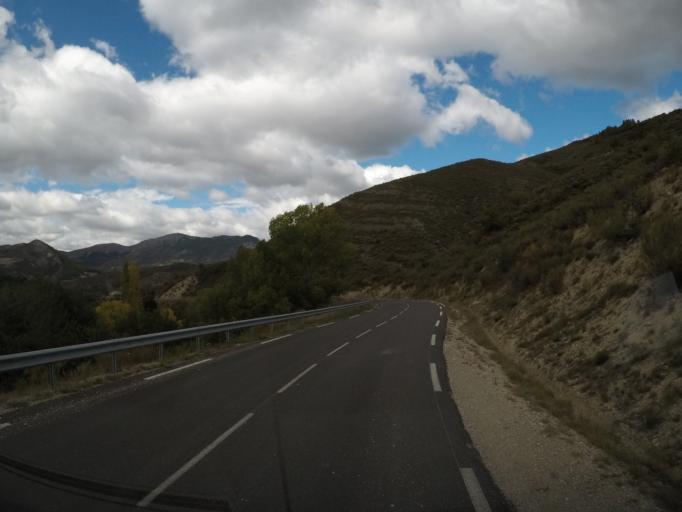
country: FR
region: Provence-Alpes-Cote d'Azur
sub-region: Departement du Vaucluse
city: Sault
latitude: 44.1826
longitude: 5.5588
